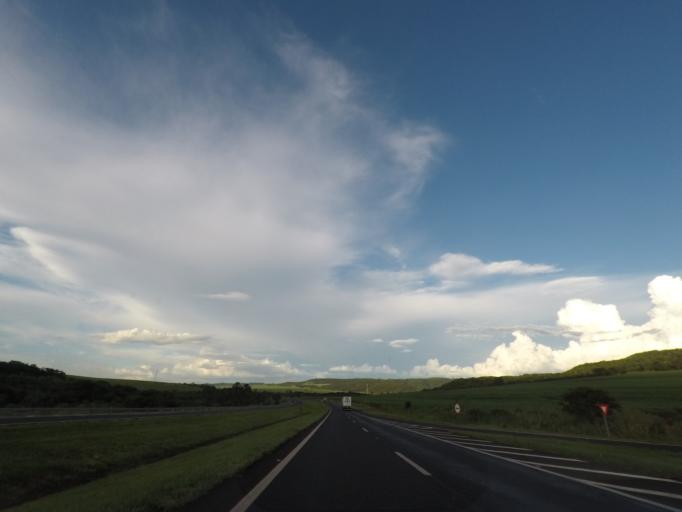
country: BR
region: Sao Paulo
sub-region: Ituverava
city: Ituverava
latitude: -20.2395
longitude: -47.7946
